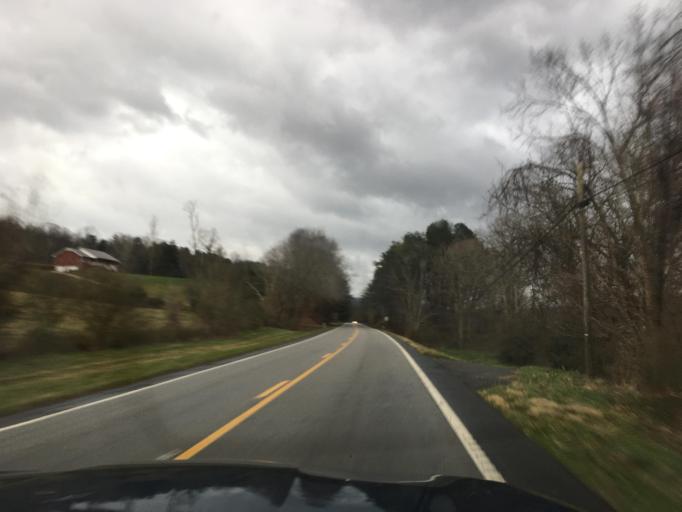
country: US
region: Tennessee
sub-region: Cumberland County
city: Lake Tansi
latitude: 35.8553
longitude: -84.9196
